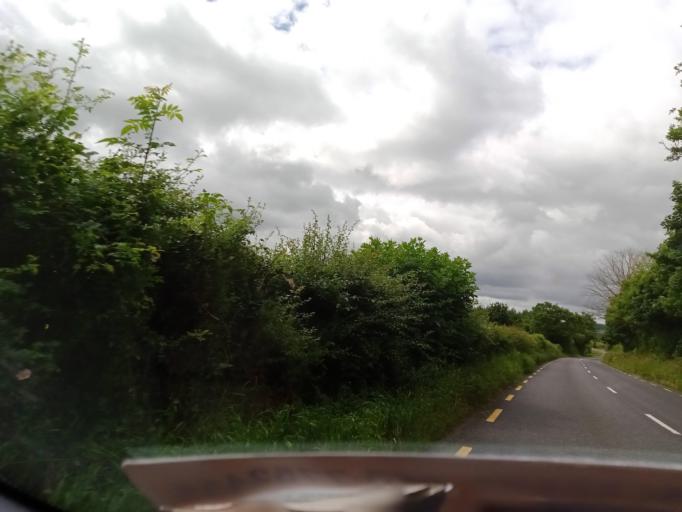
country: IE
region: Leinster
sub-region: Kilkenny
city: Thomastown
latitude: 52.4776
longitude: -7.2575
